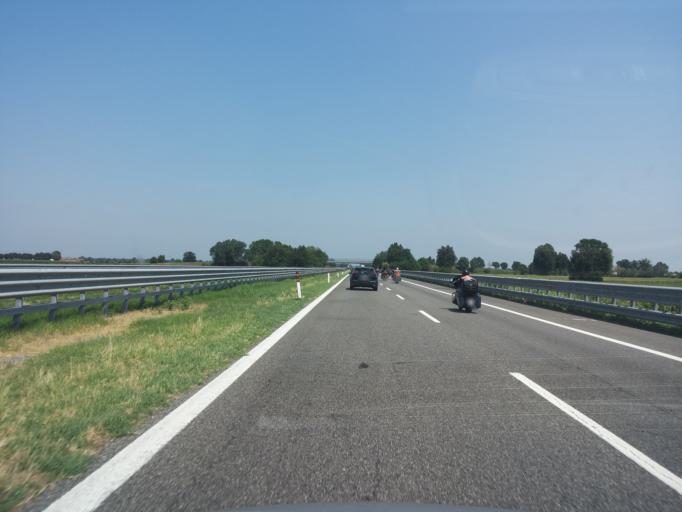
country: IT
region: Lombardy
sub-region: Provincia di Cremona
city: Dosimo
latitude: 45.1814
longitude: 10.0904
